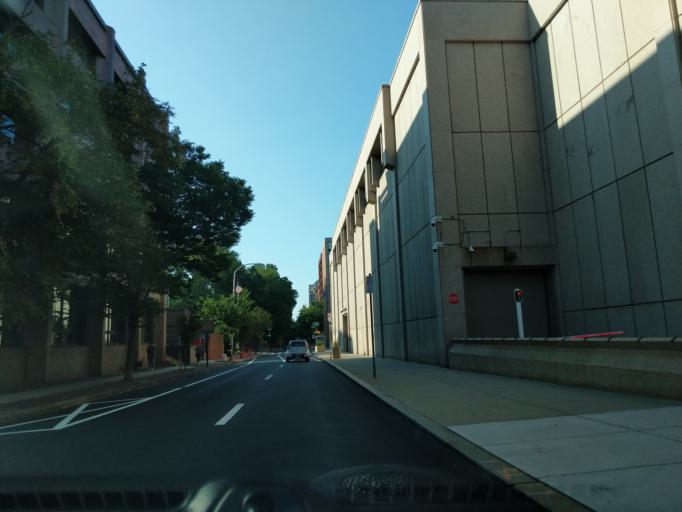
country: US
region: Pennsylvania
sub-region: Philadelphia County
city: Philadelphia
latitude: 39.9536
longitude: -75.1466
